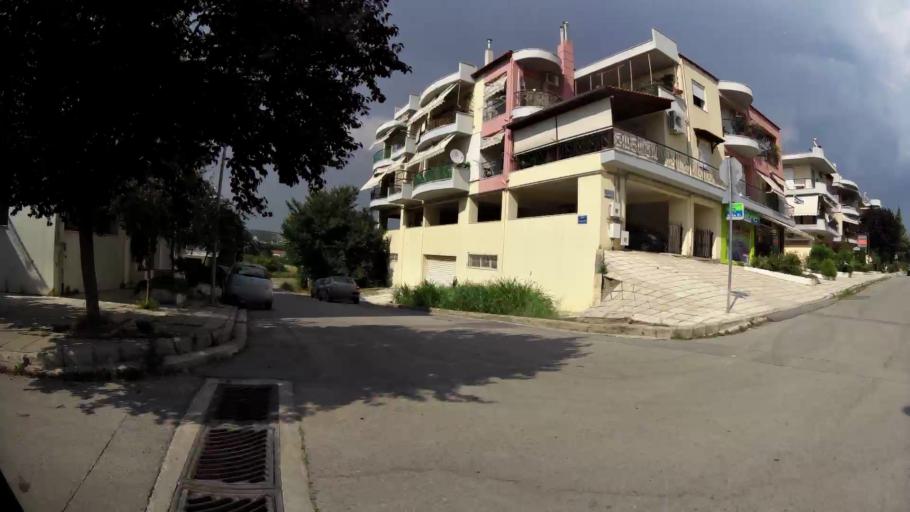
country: GR
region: Central Macedonia
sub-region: Nomos Thessalonikis
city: Polichni
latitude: 40.6686
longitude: 22.9496
